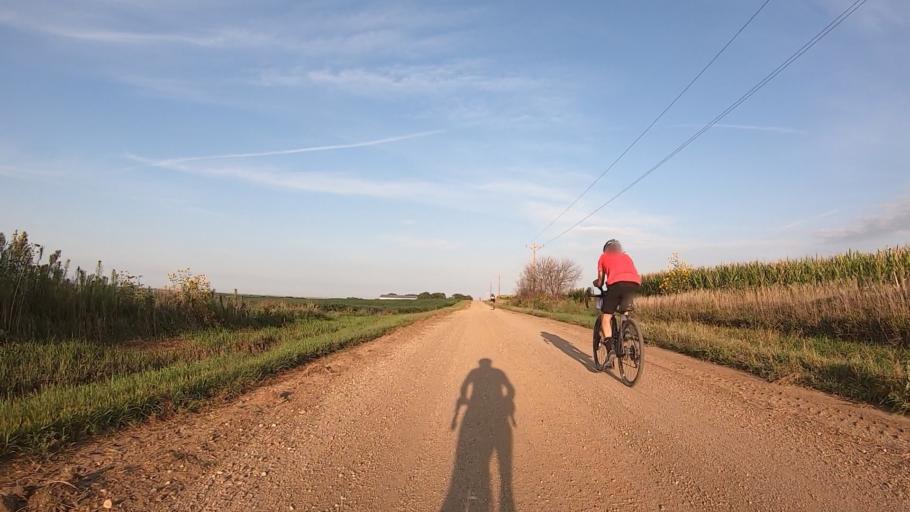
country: US
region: Kansas
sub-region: Marshall County
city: Marysville
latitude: 39.7694
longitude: -96.7415
